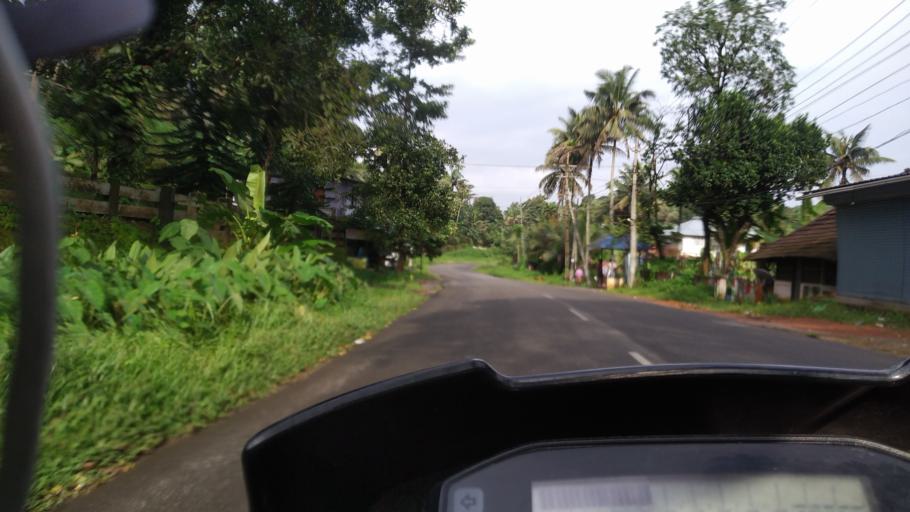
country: IN
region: Kerala
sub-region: Ernakulam
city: Kotamangalam
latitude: 10.0522
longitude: 76.7044
